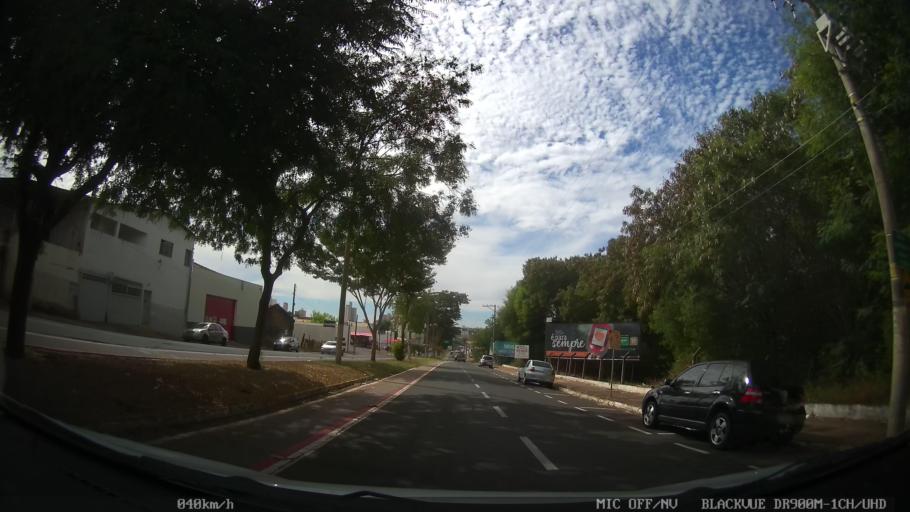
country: BR
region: Sao Paulo
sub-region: Catanduva
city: Catanduva
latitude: -21.1490
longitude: -48.9769
